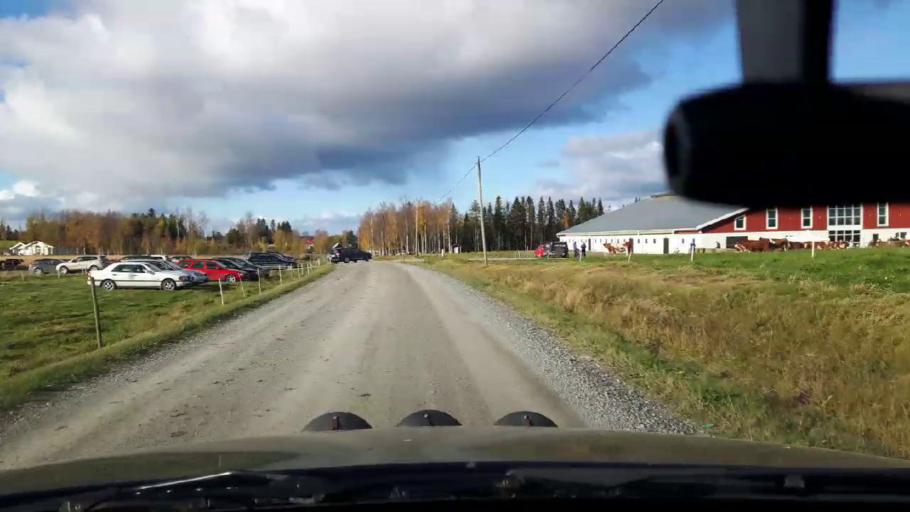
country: SE
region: Jaemtland
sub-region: Bergs Kommun
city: Hoverberg
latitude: 63.0619
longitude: 14.2322
